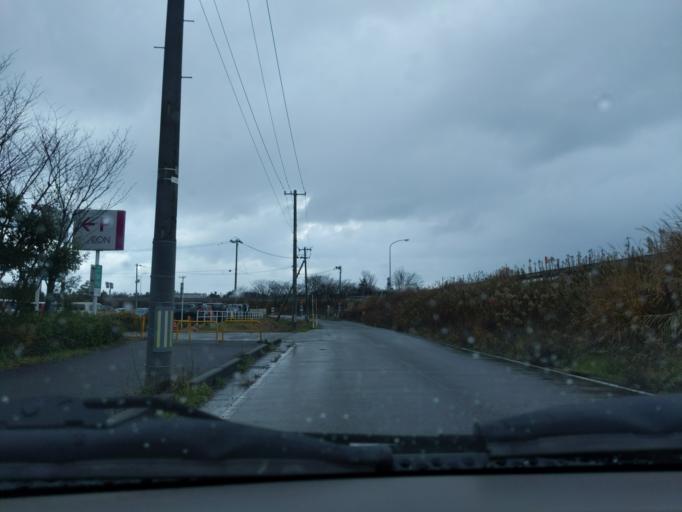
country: JP
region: Niigata
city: Kameda-honcho
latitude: 37.8775
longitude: 139.0832
